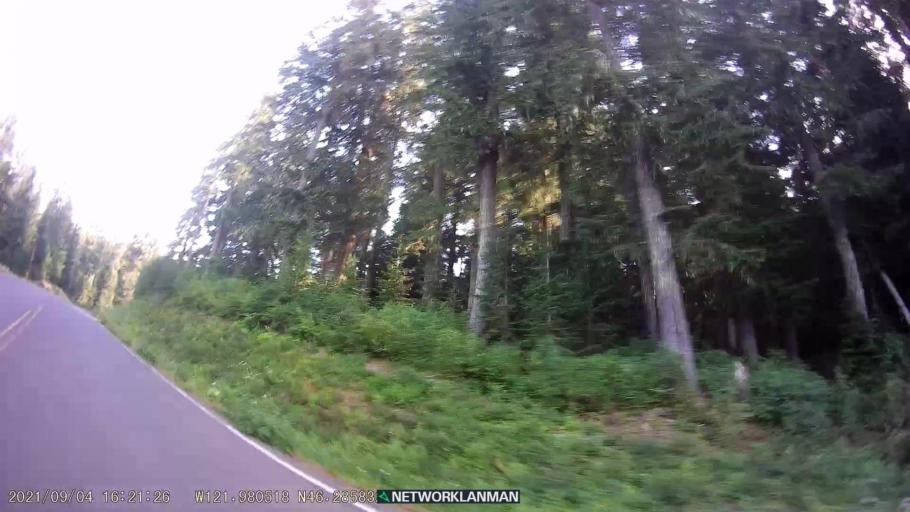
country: US
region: Washington
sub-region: Lewis County
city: Morton
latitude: 46.2856
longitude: -121.9802
